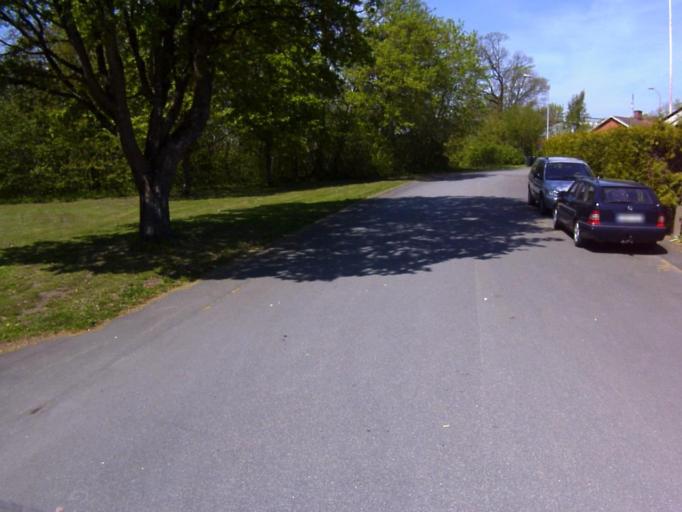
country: SE
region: Skane
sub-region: Kristianstads Kommun
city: Onnestad
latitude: 55.9301
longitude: 13.9847
